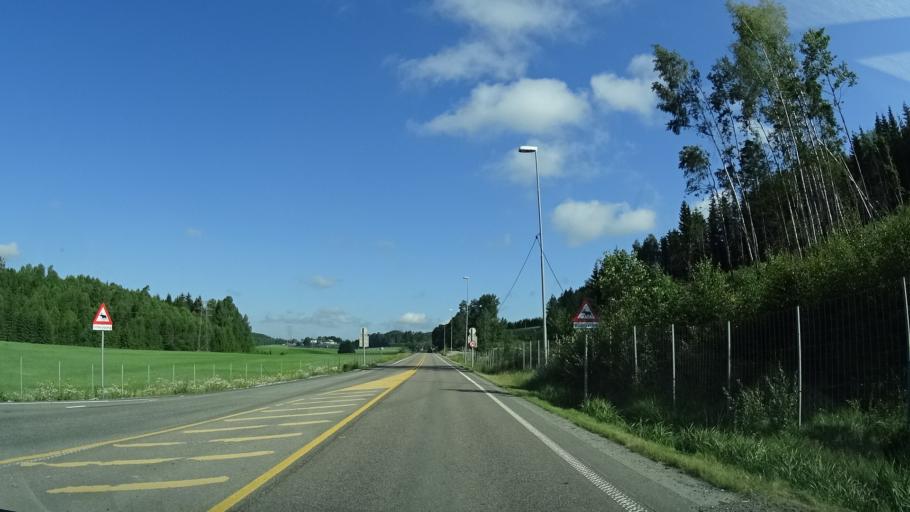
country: NO
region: Ostfold
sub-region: Hobol
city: Elvestad
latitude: 59.6479
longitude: 10.9234
